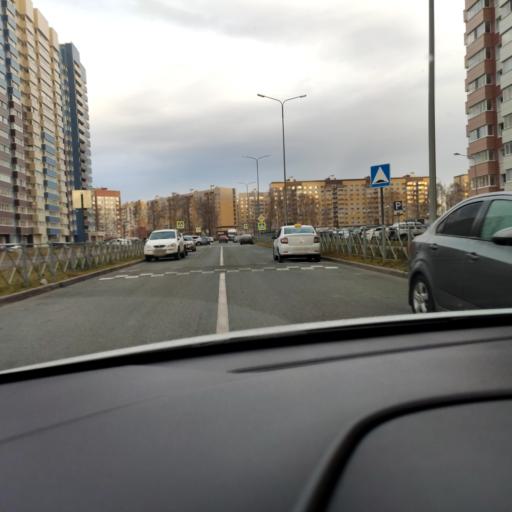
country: RU
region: Tatarstan
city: Osinovo
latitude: 55.8665
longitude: 48.8818
